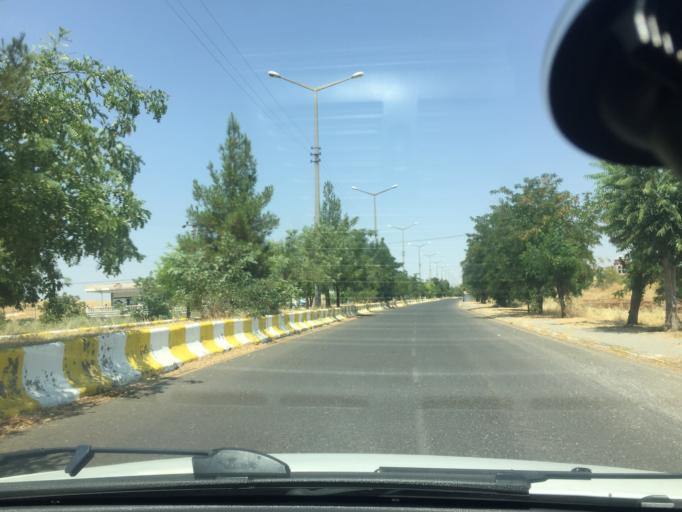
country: TR
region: Mardin
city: Kindirip
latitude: 37.4571
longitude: 41.2240
